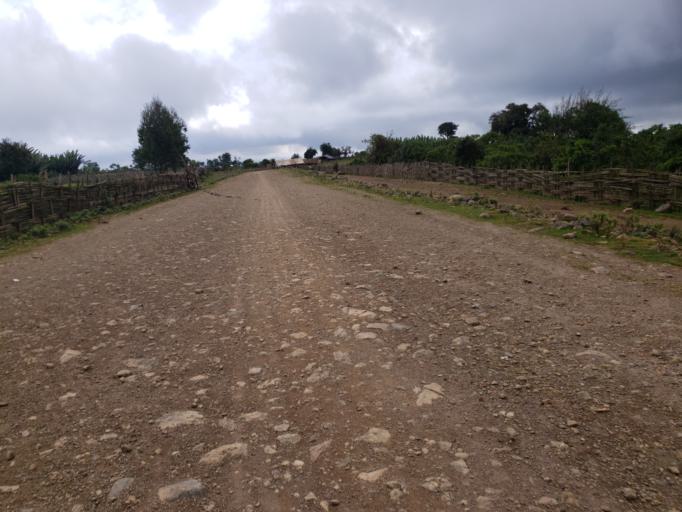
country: ET
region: Oromiya
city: Dodola
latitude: 6.7025
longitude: 39.3730
